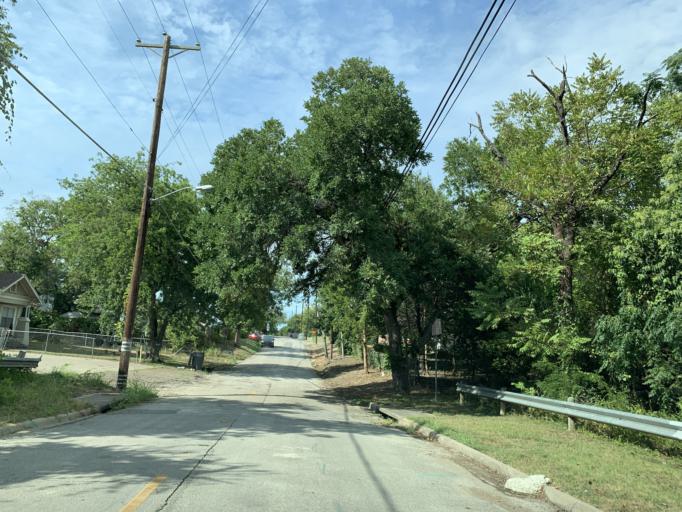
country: US
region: Texas
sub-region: Dallas County
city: Cockrell Hill
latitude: 32.7359
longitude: -96.8400
